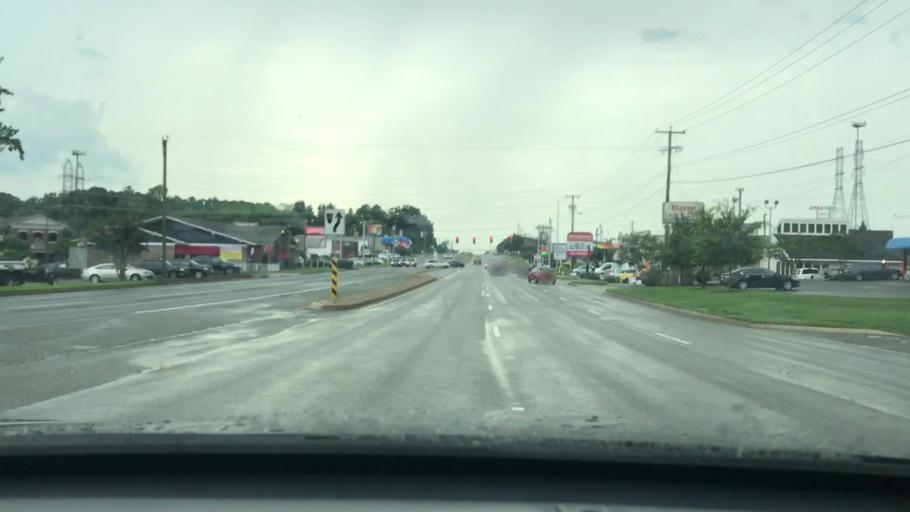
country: US
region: Virginia
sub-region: Henrico County
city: Laurel
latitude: 37.6317
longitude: -77.5380
